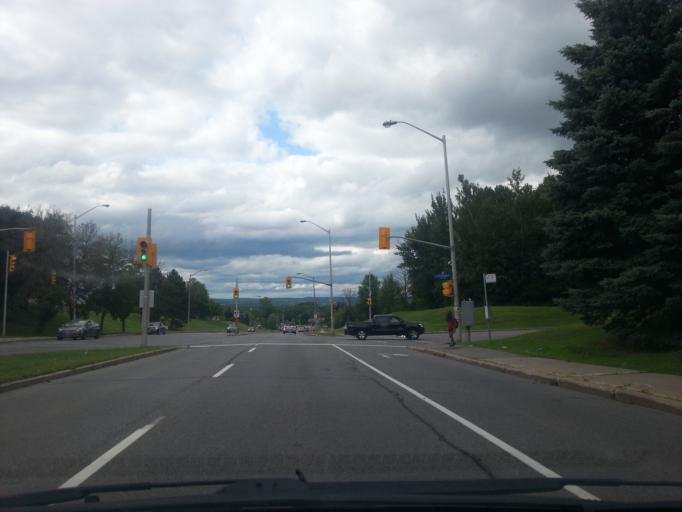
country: CA
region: Quebec
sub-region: Outaouais
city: Gatineau
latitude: 45.4649
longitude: -75.5278
